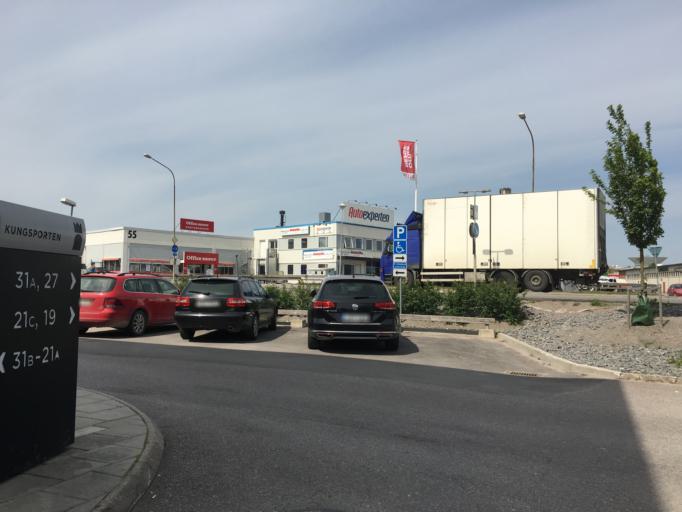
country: SE
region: Uppsala
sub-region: Uppsala Kommun
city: Uppsala
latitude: 59.8465
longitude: 17.6742
